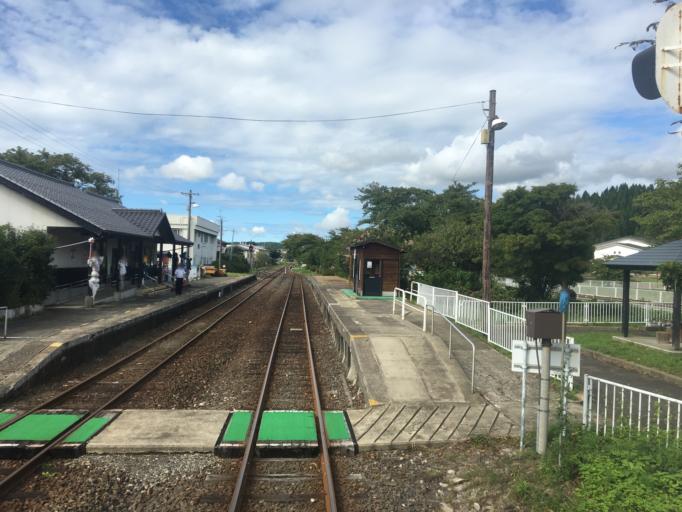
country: JP
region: Yamagata
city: Yuza
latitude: 39.3124
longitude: 140.1130
